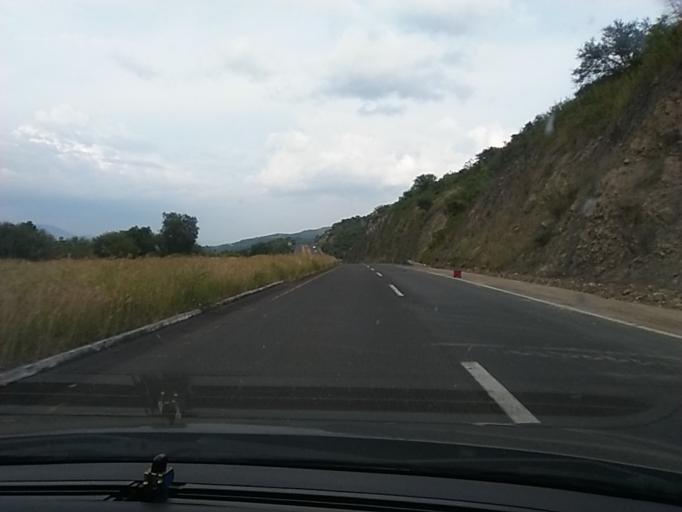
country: MX
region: Mexico
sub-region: Chapultepec
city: Chucandiro
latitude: 19.8833
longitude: -101.3412
